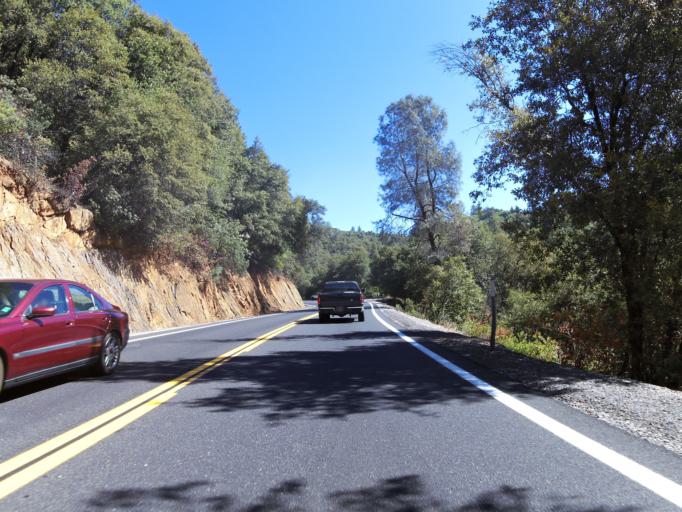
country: US
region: California
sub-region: Calaveras County
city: Murphys
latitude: 38.1532
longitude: -120.4394
